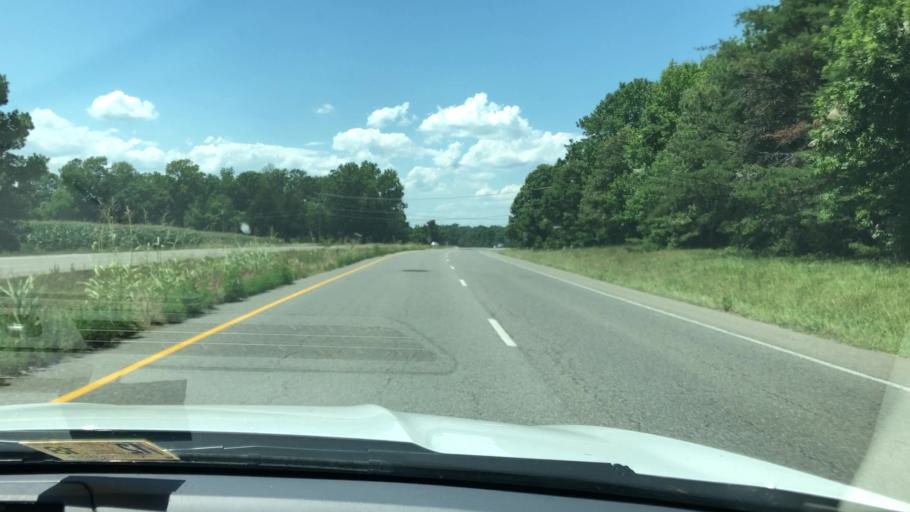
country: US
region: Virginia
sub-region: Middlesex County
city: Saluda
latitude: 37.6072
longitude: -76.5431
